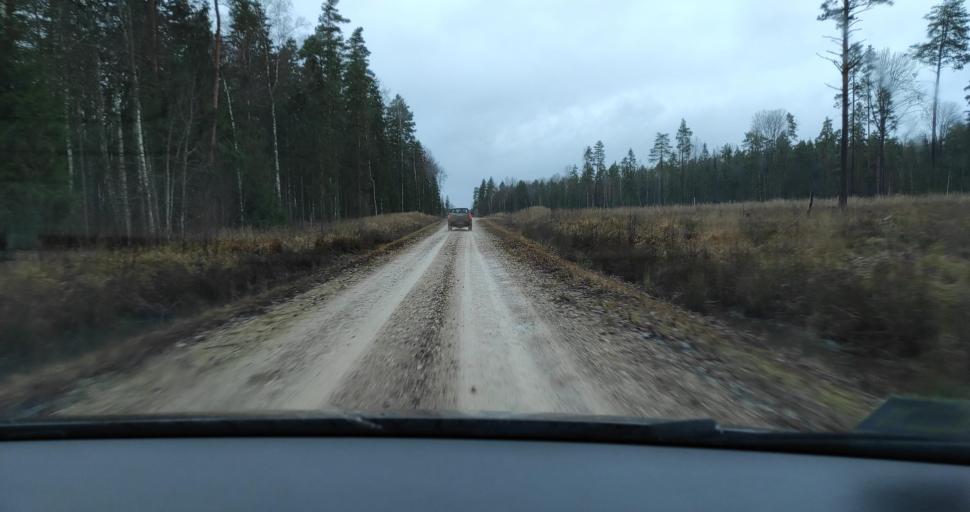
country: LV
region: Skrunda
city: Skrunda
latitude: 56.5572
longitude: 22.0813
